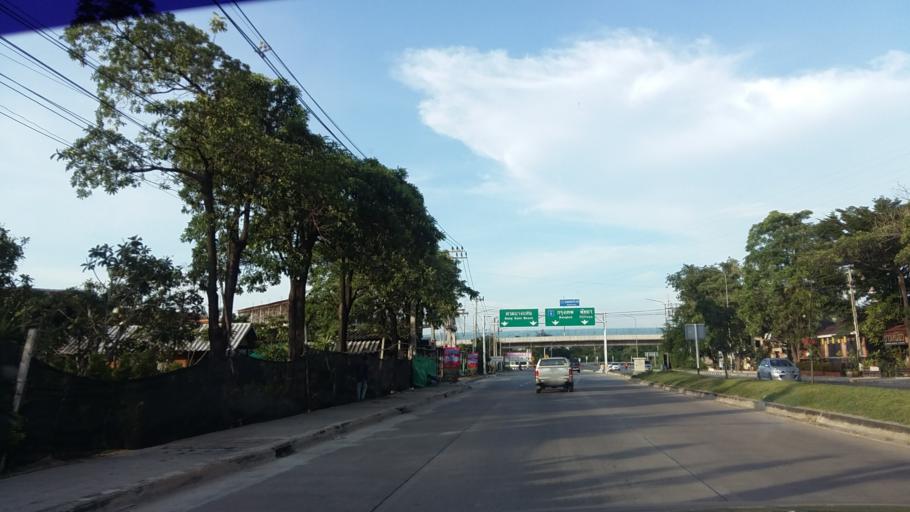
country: TH
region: Chon Buri
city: Chon Buri
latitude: 13.2884
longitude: 100.9493
